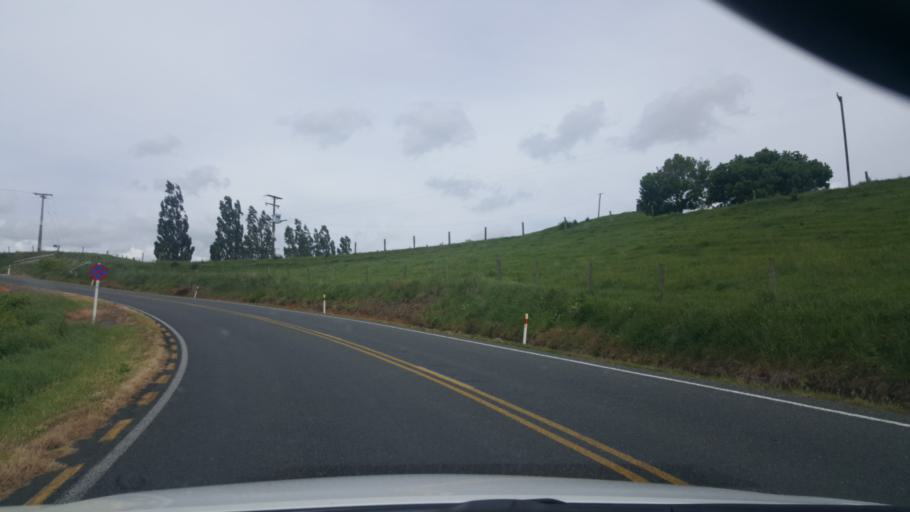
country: NZ
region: Waikato
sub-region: Matamata-Piako District
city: Matamata
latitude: -37.8770
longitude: 175.6855
